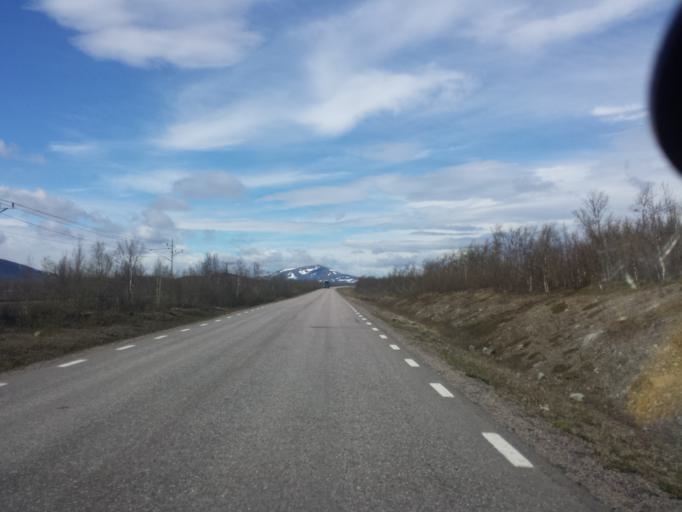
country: SE
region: Norrbotten
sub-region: Kiruna Kommun
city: Kiruna
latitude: 68.0568
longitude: 19.8274
